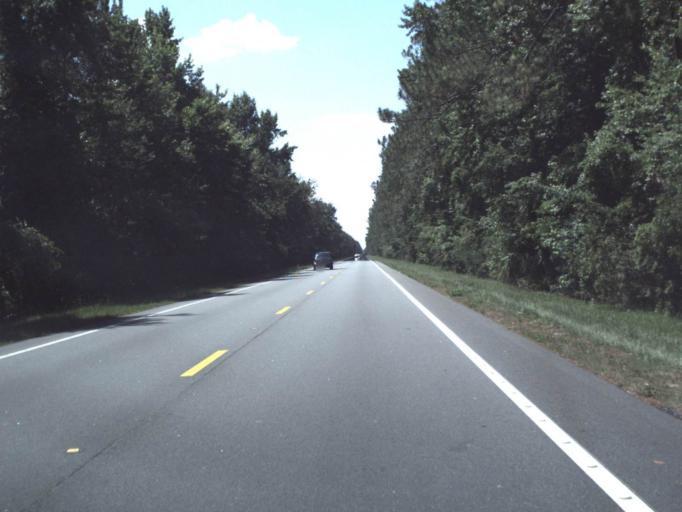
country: US
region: Florida
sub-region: Nassau County
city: Yulee
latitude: 30.6748
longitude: -81.6439
